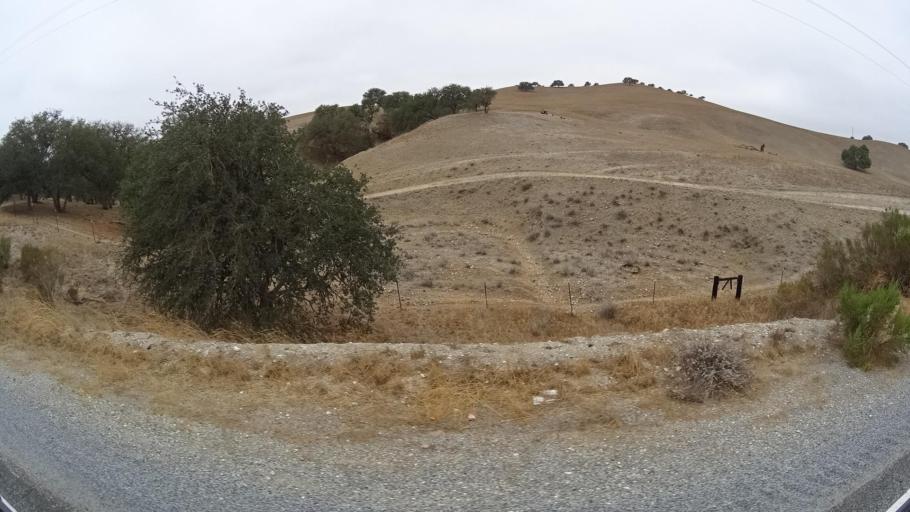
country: US
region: California
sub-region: San Luis Obispo County
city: Lake Nacimiento
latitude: 35.8712
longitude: -120.8408
